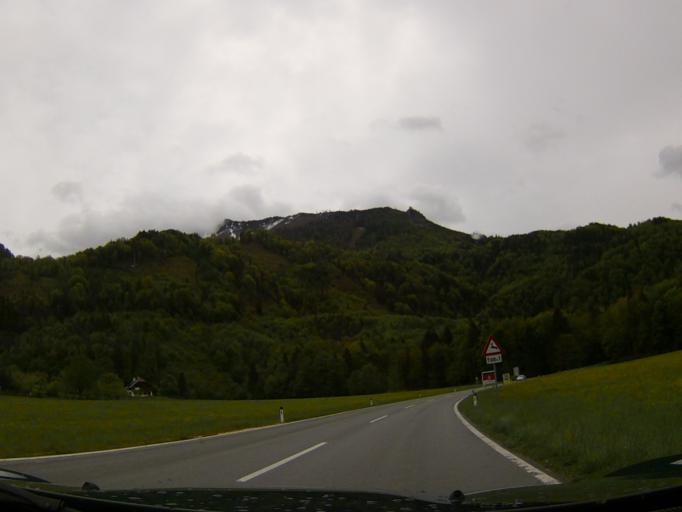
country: AT
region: Upper Austria
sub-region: Politischer Bezirk Vocklabruck
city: Innerschwand
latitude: 47.7972
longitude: 13.3986
